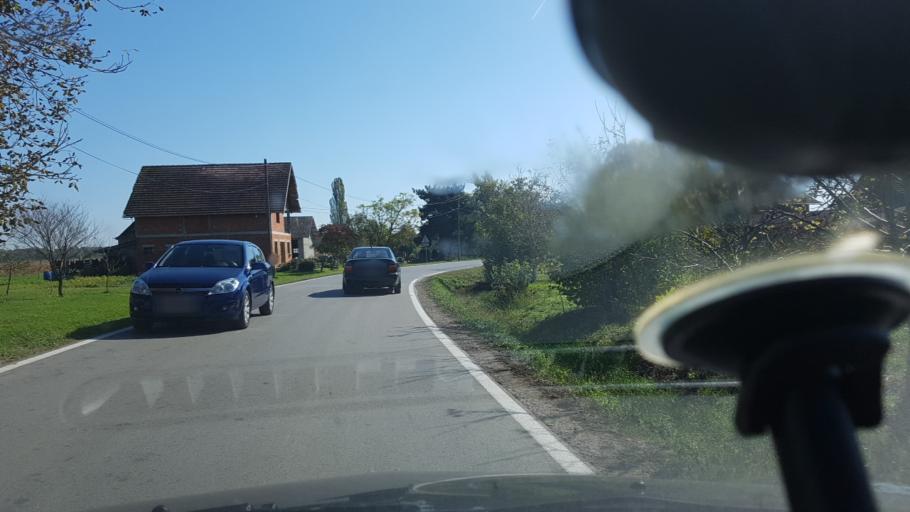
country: HR
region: Zagrebacka
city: Lupoglav
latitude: 45.7210
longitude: 16.3115
